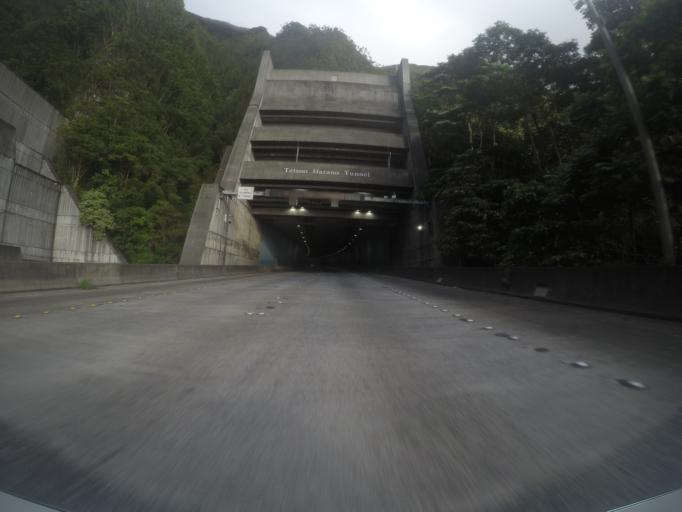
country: US
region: Hawaii
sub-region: Honolulu County
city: Kane'ohe
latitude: 21.4039
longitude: -157.8347
